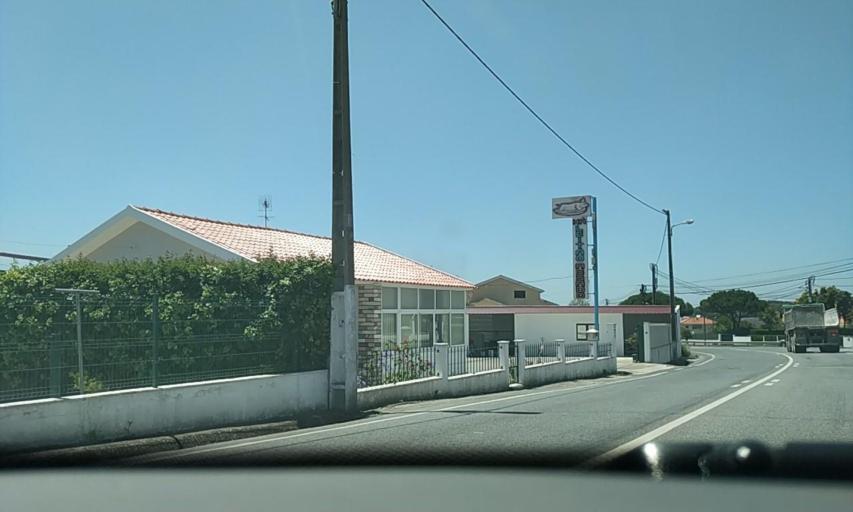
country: PT
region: Lisbon
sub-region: Sintra
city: Almargem
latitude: 38.8781
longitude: -9.2731
